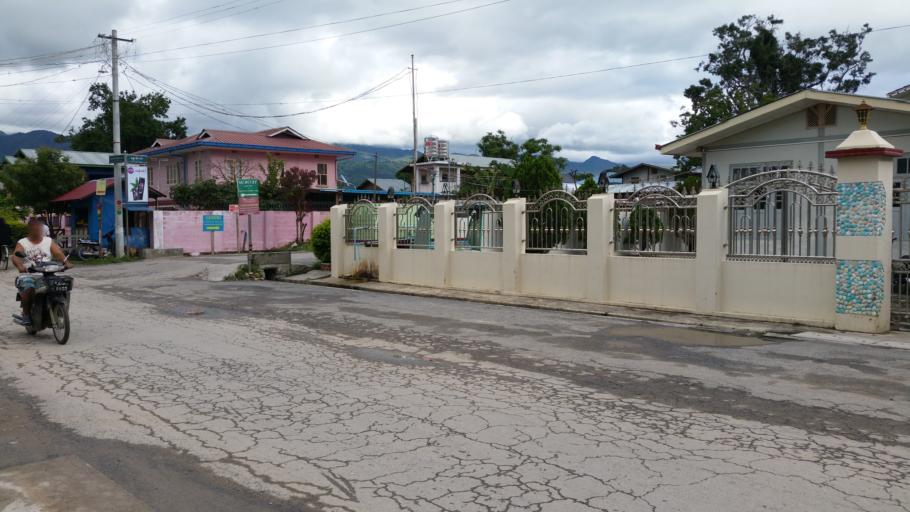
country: MM
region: Shan
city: Taunggyi
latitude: 20.6593
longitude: 96.9358
